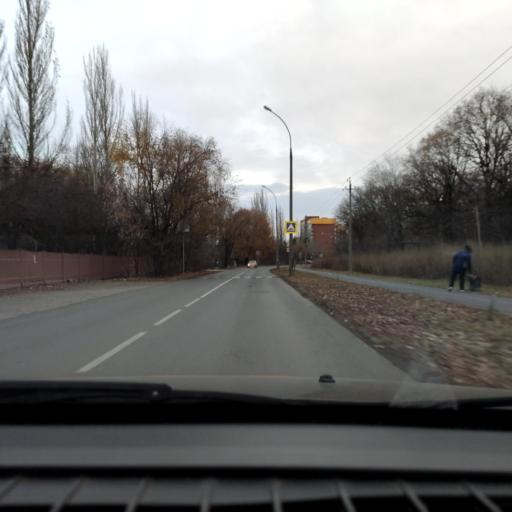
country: RU
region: Samara
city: Tol'yatti
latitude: 53.5124
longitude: 49.3096
